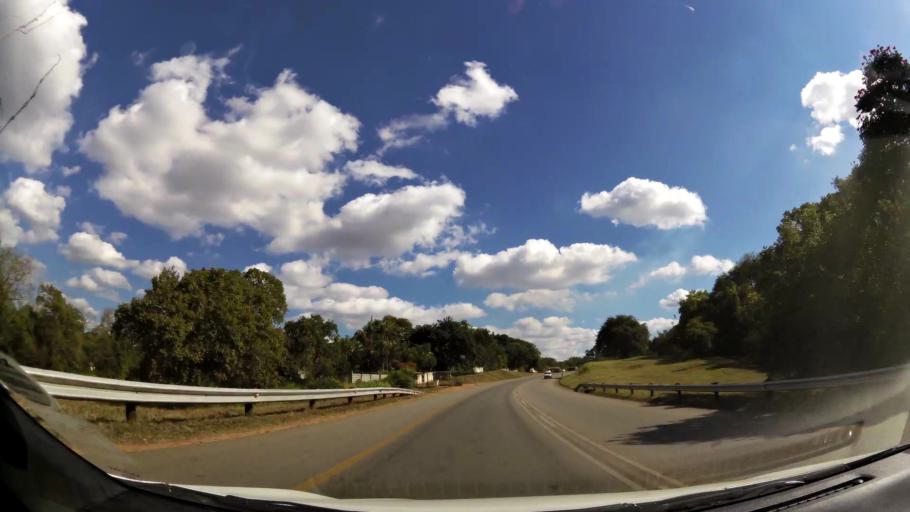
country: ZA
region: Limpopo
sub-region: Mopani District Municipality
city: Tzaneen
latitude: -23.8298
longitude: 30.1499
